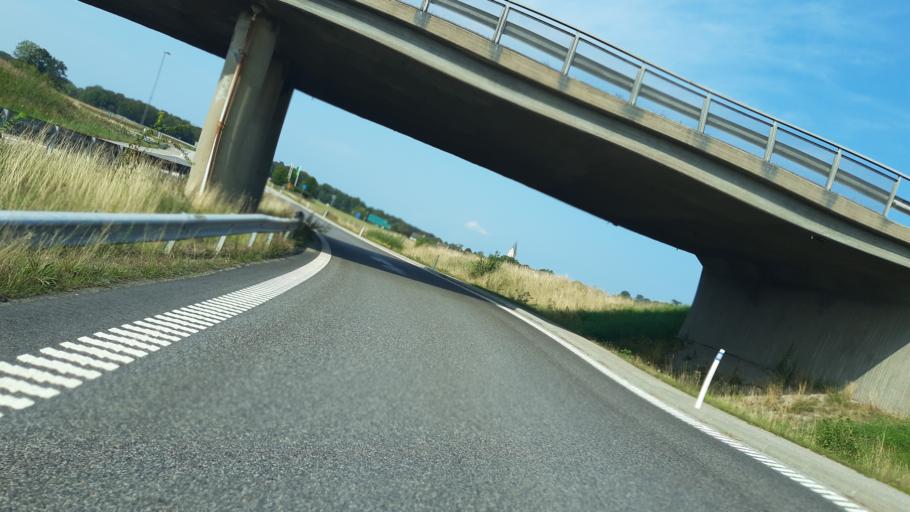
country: SE
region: Blekinge
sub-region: Ronneby Kommun
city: Brakne-Hoby
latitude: 56.2183
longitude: 15.1197
